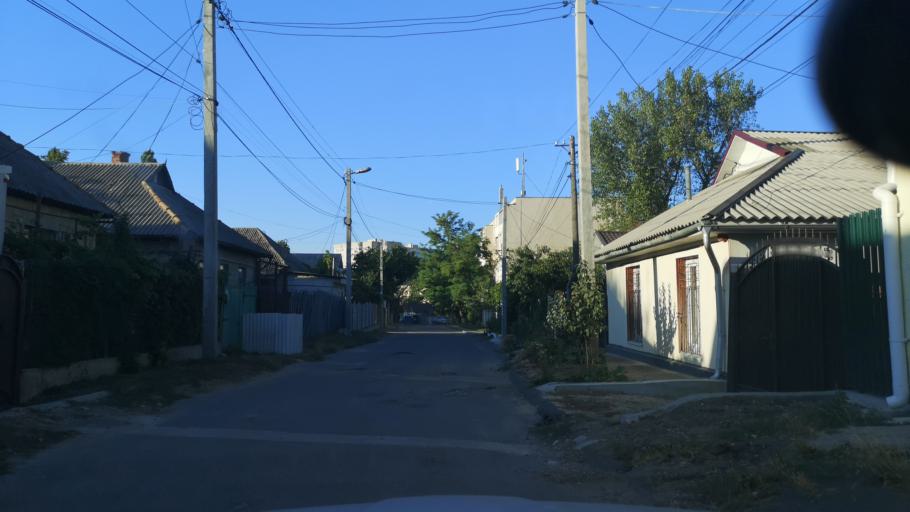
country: MD
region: Chisinau
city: Chisinau
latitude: 46.9878
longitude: 28.8803
